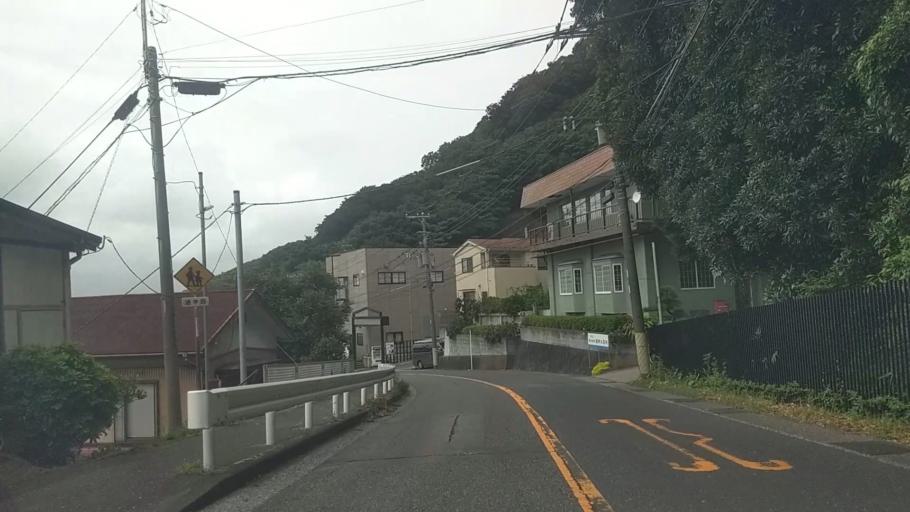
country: JP
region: Kanagawa
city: Yokosuka
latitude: 35.2576
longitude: 139.7191
